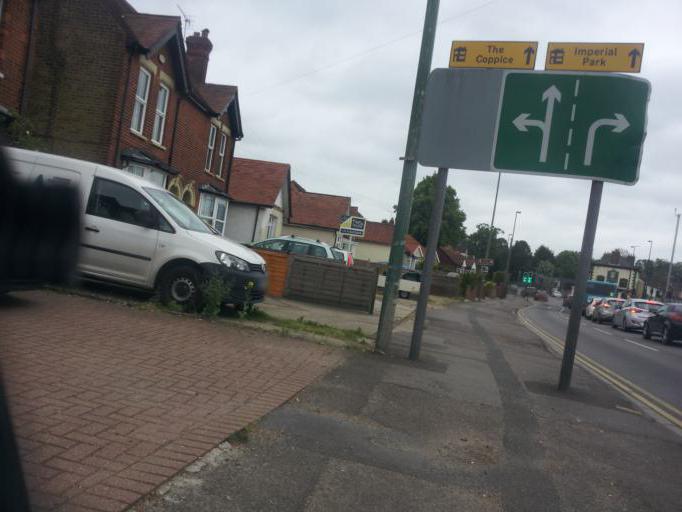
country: GB
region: England
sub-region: Kent
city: Maidstone
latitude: 51.2584
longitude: 0.5311
